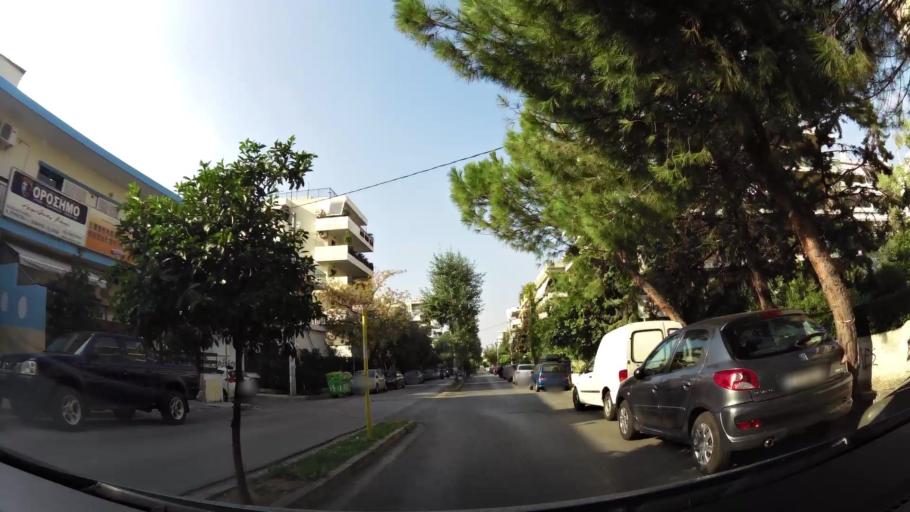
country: GR
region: Attica
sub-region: Nomarchia Athinas
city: Cholargos
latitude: 38.0052
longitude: 23.8076
